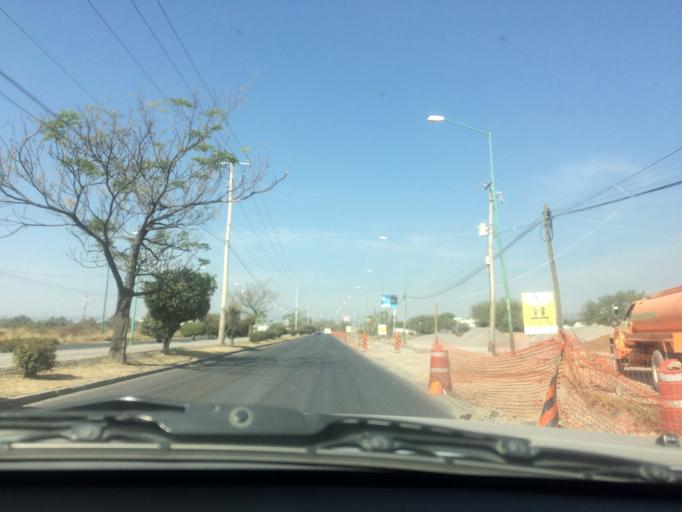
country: MX
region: Guanajuato
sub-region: Leon
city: Medina
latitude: 21.1537
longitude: -101.6381
